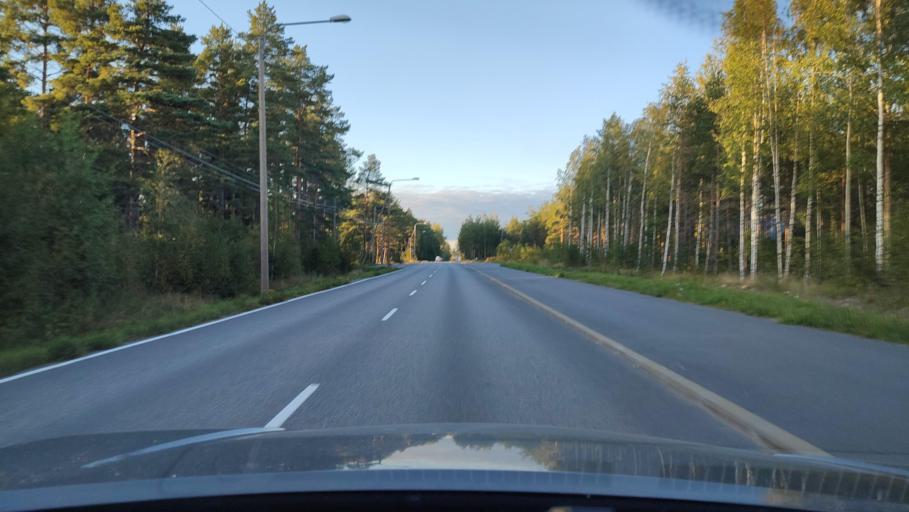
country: FI
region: Ostrobothnia
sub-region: Sydosterbotten
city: Kristinestad
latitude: 62.2344
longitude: 21.5209
